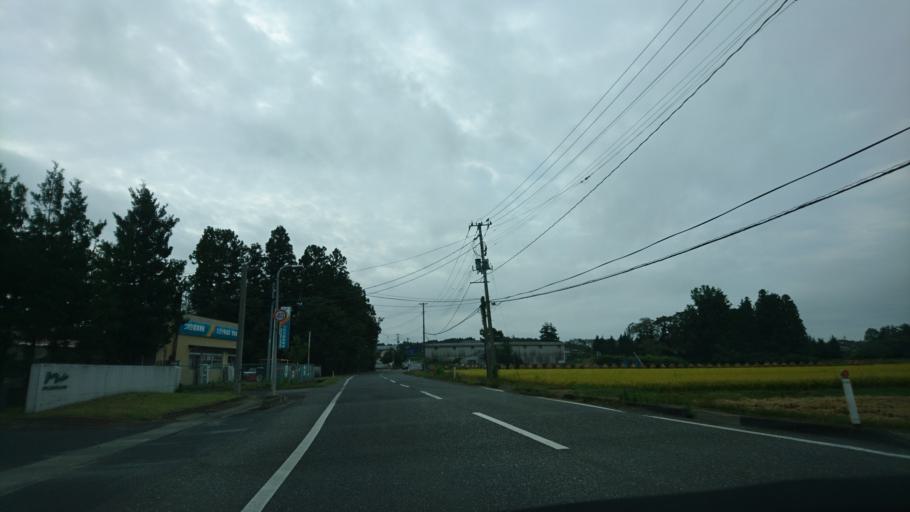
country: JP
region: Iwate
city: Ichinoseki
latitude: 38.7834
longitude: 141.1164
